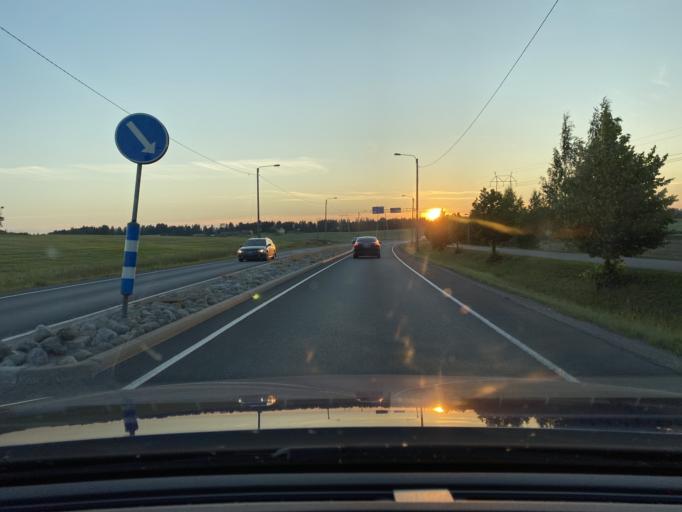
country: FI
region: Pirkanmaa
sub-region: Luoteis-Pirkanmaa
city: Ikaalinen
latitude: 61.7582
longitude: 23.0305
